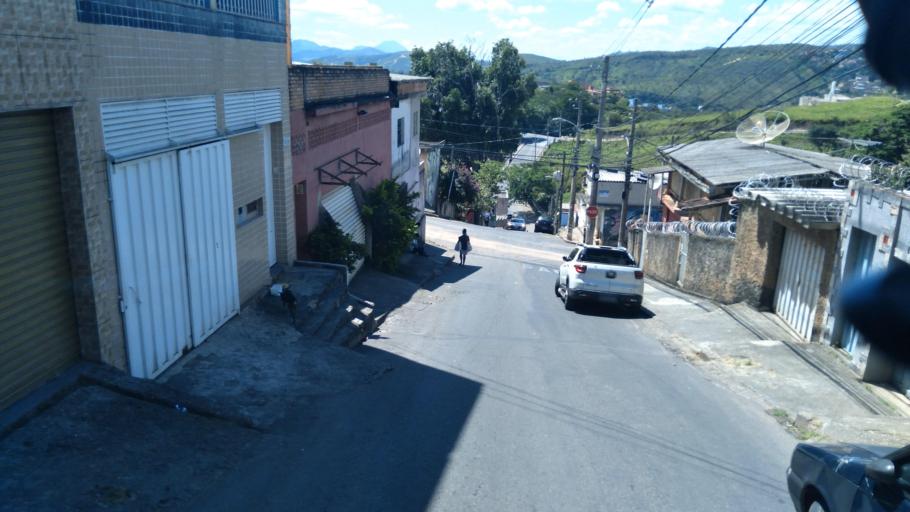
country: BR
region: Minas Gerais
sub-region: Belo Horizonte
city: Belo Horizonte
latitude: -19.9091
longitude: -43.8889
